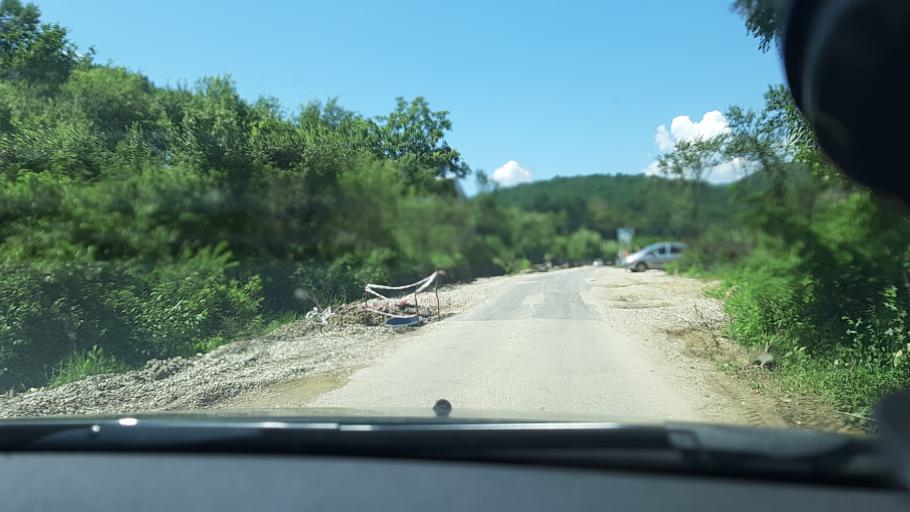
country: RO
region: Hunedoara
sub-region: Comuna Teliucu Inferior
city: Teliucu Inferior
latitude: 45.6875
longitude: 22.8616
